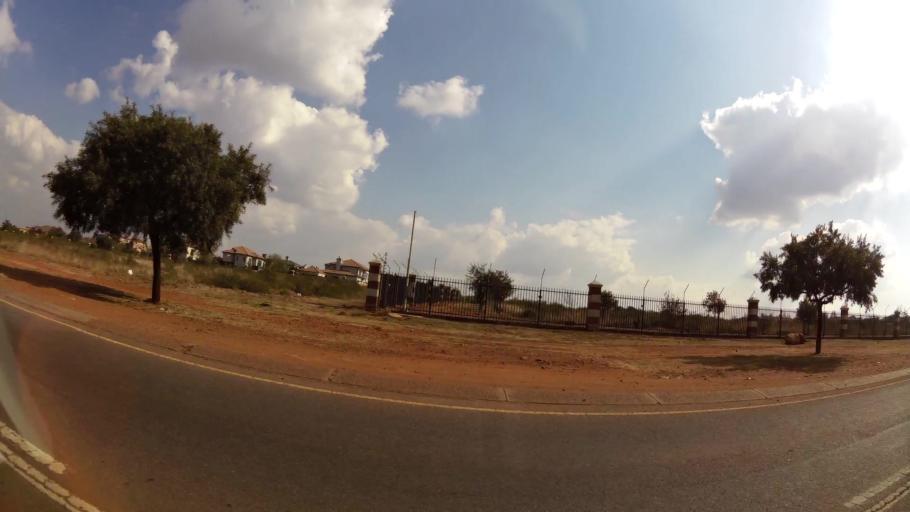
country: ZA
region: Gauteng
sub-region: City of Tshwane Metropolitan Municipality
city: Centurion
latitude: -25.8578
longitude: 28.2478
